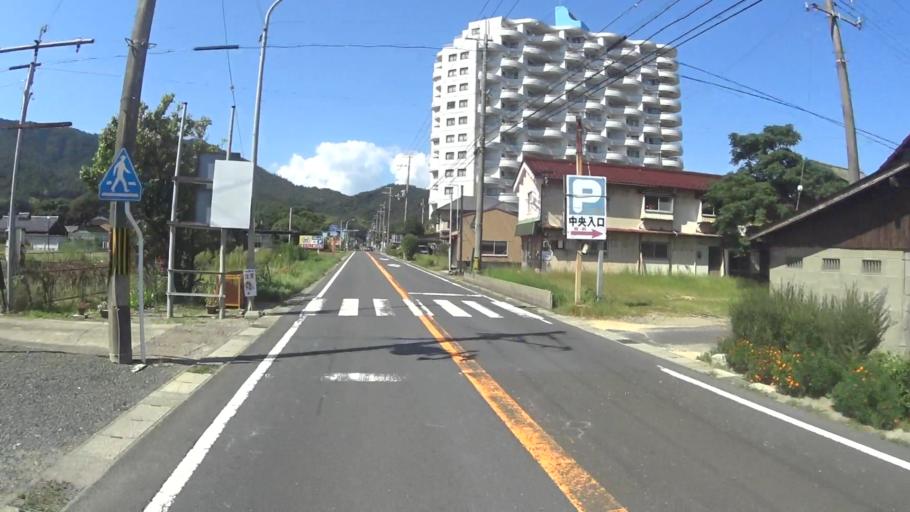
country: JP
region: Kyoto
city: Maizuru
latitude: 35.5196
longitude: 135.2803
